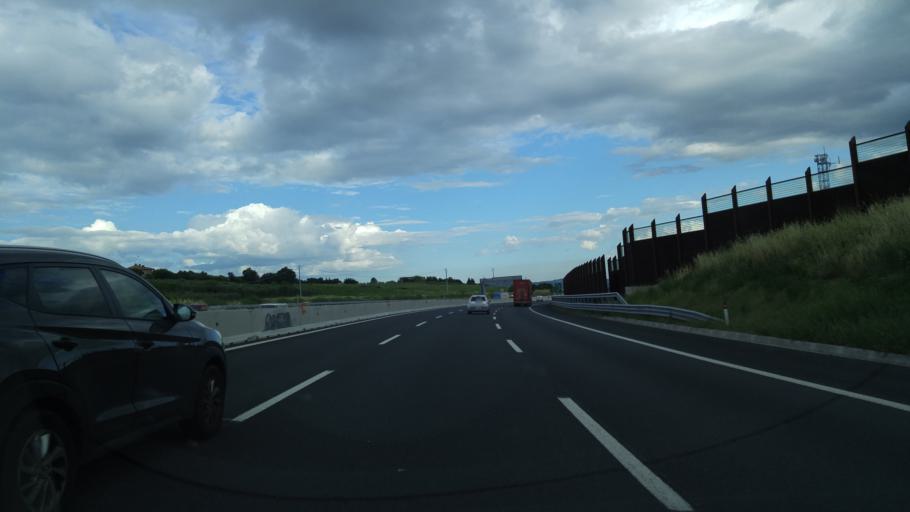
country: IT
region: Emilia-Romagna
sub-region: Provincia di Rimini
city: Riccione
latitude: 43.9779
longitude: 12.6589
